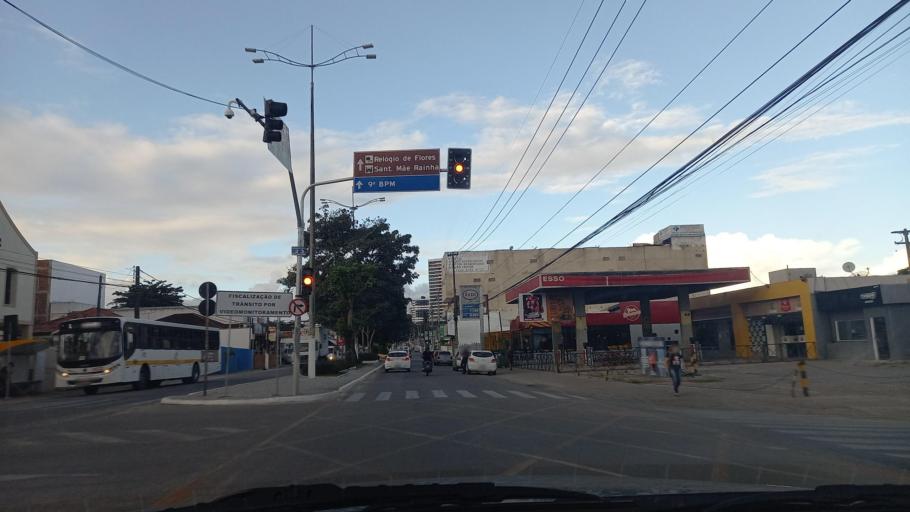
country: BR
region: Pernambuco
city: Garanhuns
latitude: -8.8841
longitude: -36.4812
